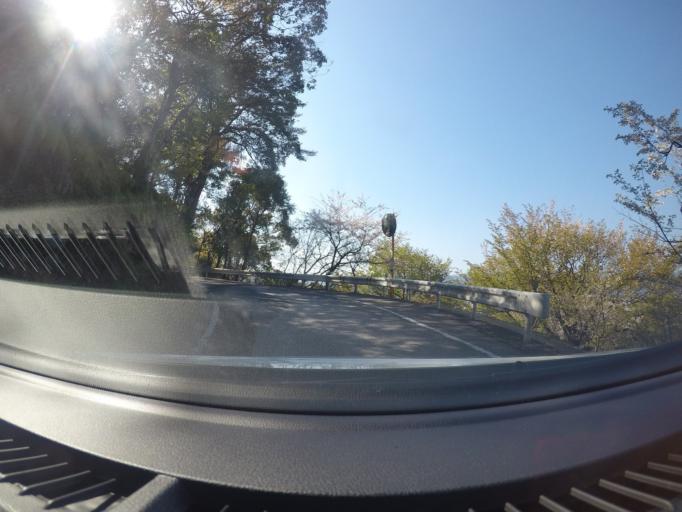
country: JP
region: Kochi
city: Kochi-shi
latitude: 33.5494
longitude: 133.5748
